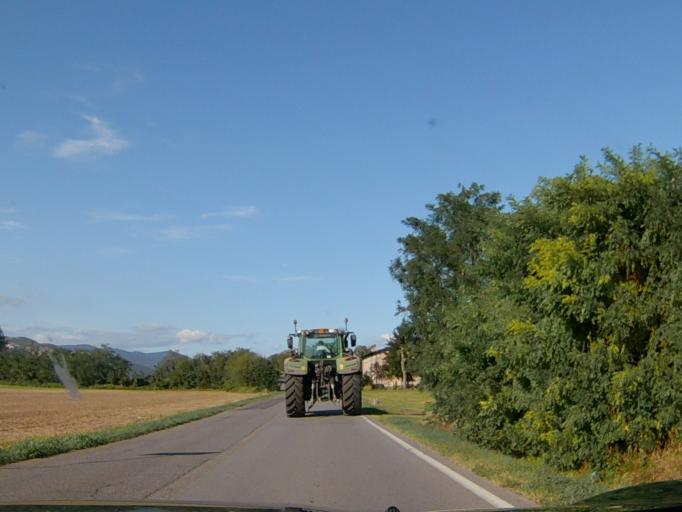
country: IT
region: Lombardy
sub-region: Provincia di Brescia
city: Molinetto
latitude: 45.4817
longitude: 10.3329
